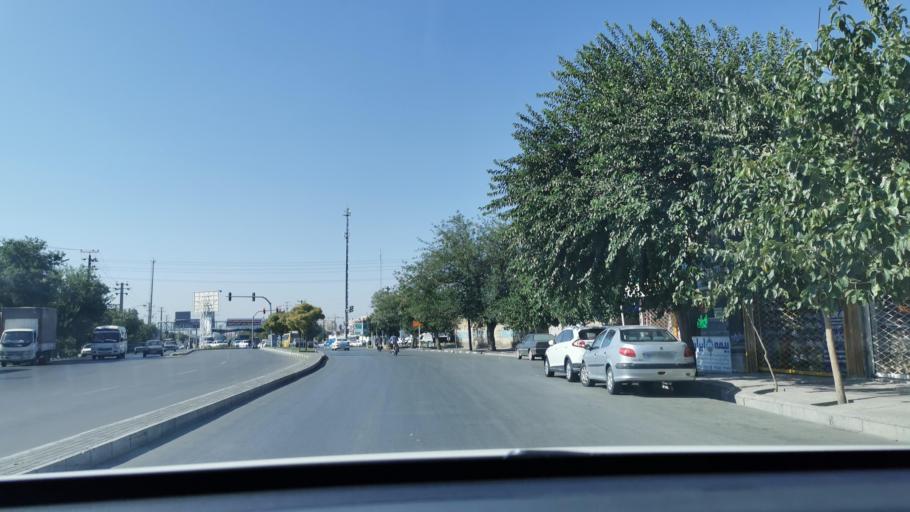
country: IR
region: Razavi Khorasan
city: Mashhad
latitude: 36.3386
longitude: 59.6265
